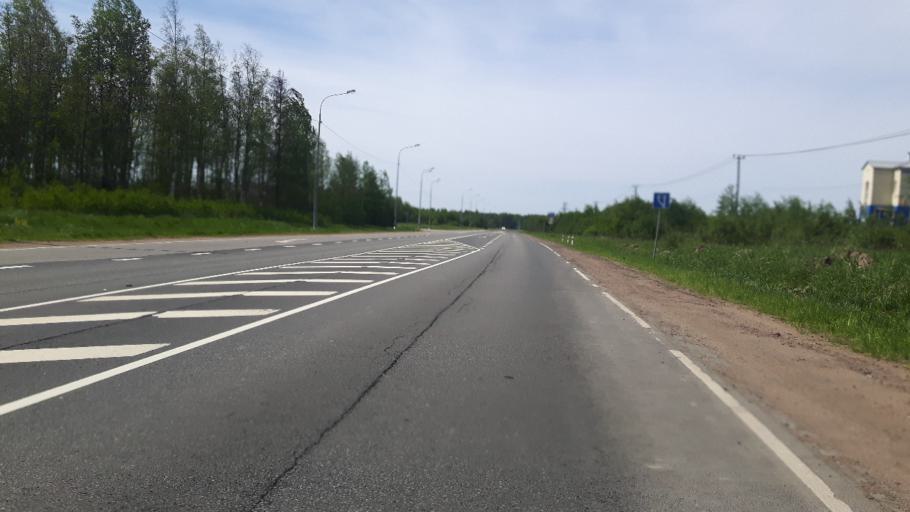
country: RU
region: Leningrad
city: Ust'-Luga
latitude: 59.6550
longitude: 28.3823
